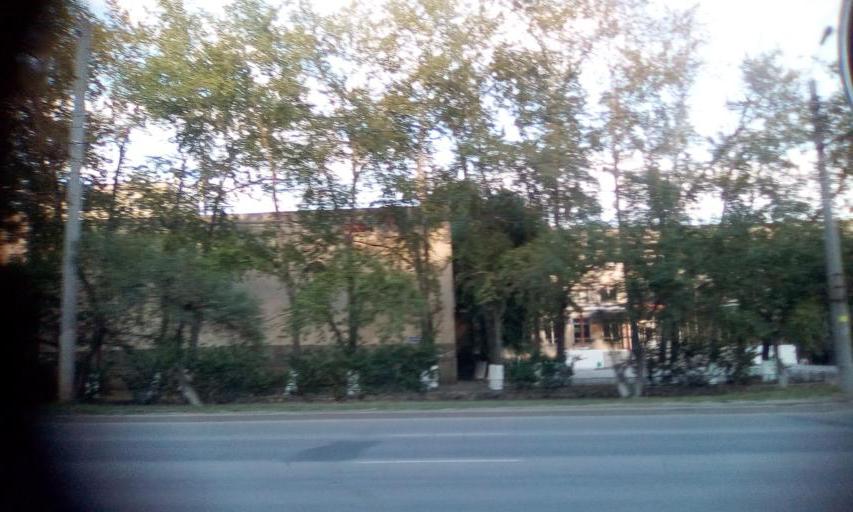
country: RU
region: Chelyabinsk
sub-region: Gorod Chelyabinsk
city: Chelyabinsk
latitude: 55.1219
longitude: 61.3633
